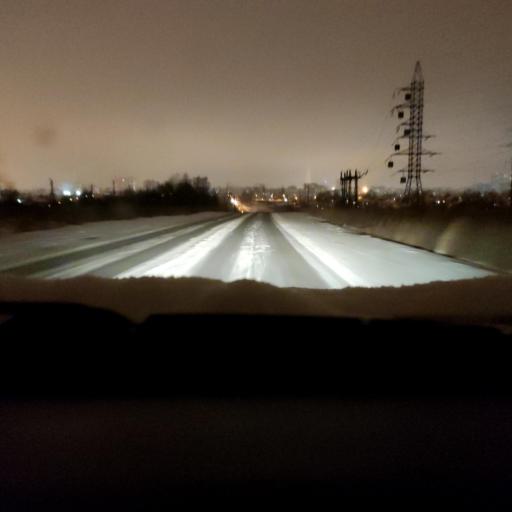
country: RU
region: Perm
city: Perm
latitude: 58.0157
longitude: 56.3314
